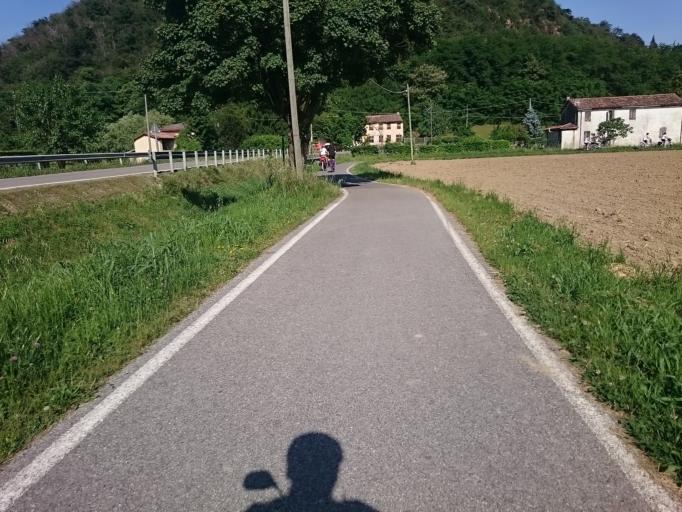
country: IT
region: Veneto
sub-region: Provincia di Padova
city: Torreglia
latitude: 45.3530
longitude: 11.7461
